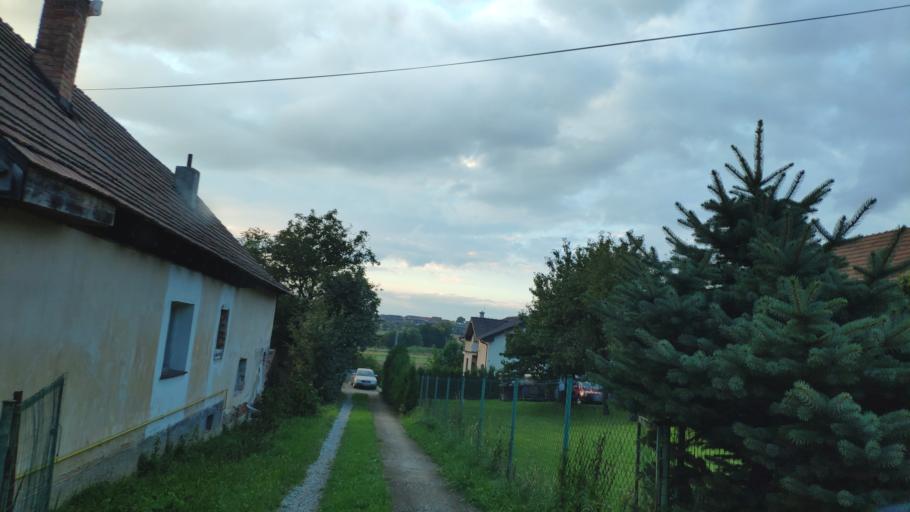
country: SK
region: Kosicky
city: Kosice
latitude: 48.8331
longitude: 21.3181
